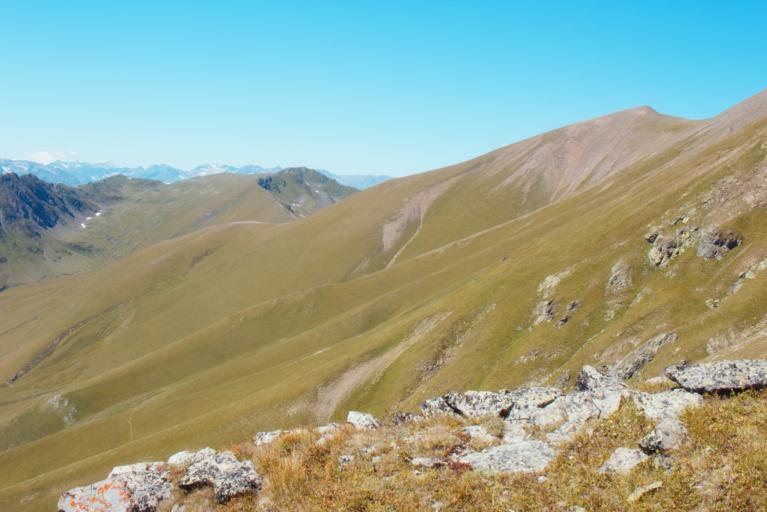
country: RU
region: Karachayevo-Cherkesiya
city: Mednogorskiy
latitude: 43.6144
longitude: 41.0951
